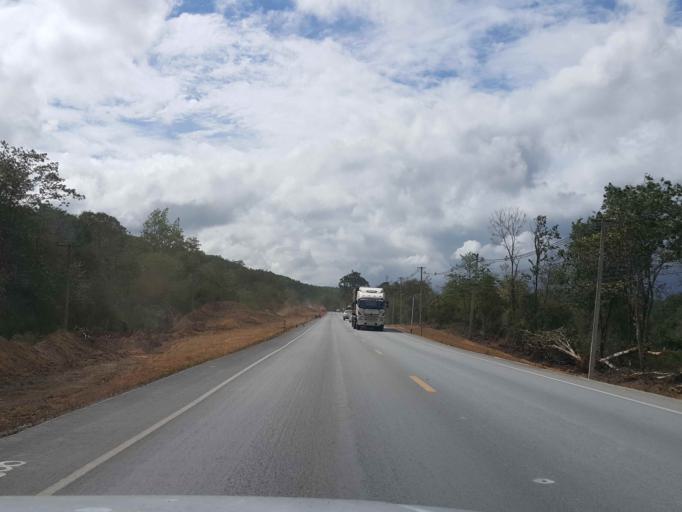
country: TH
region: Tak
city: Tak
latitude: 16.7984
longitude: 99.0070
